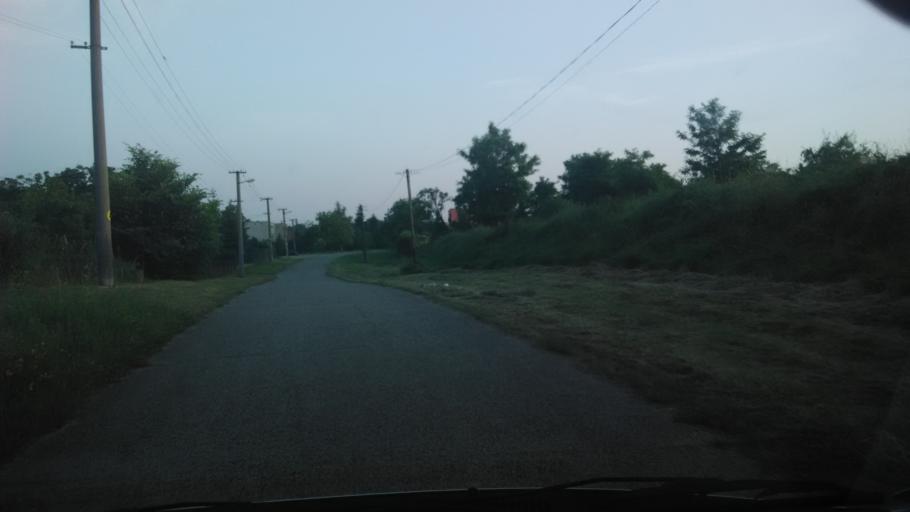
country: SK
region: Nitriansky
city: Levice
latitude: 48.1341
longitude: 18.4583
